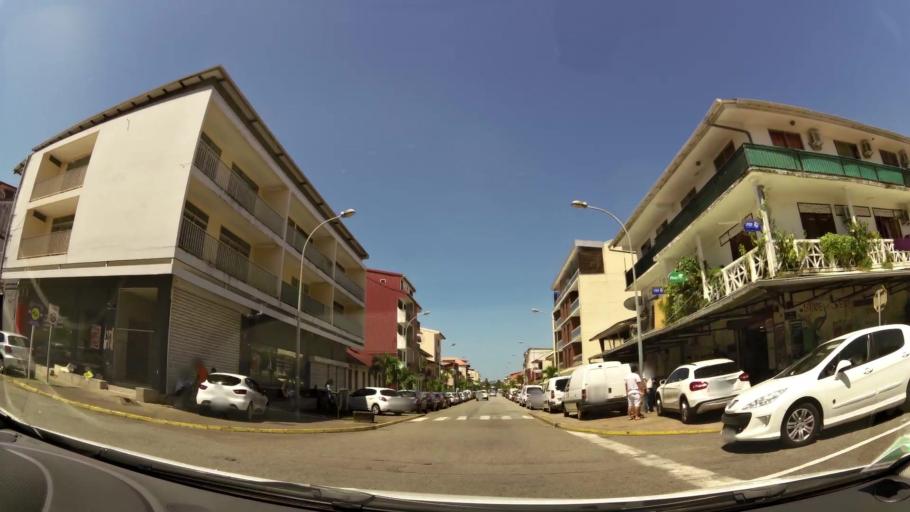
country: GF
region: Guyane
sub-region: Guyane
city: Cayenne
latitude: 4.9416
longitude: -52.3254
